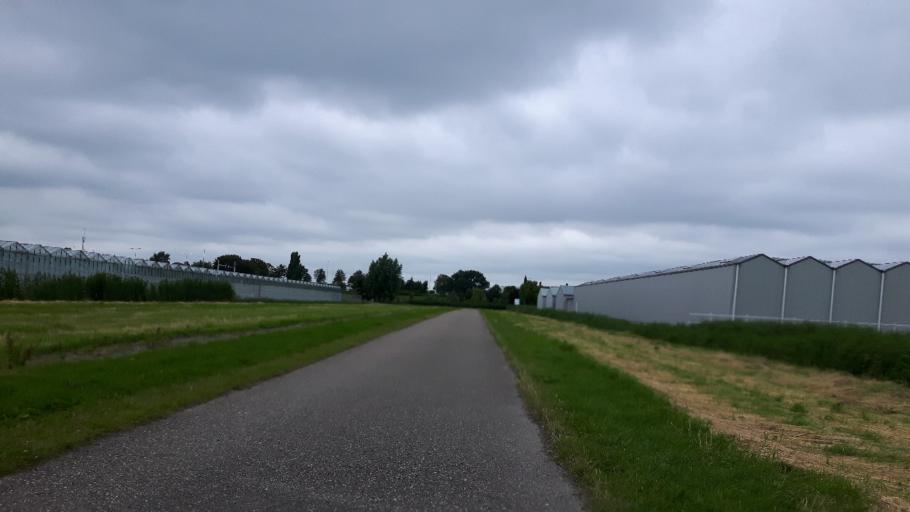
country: NL
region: South Holland
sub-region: Gemeente Lansingerland
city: Bleiswijk
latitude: 51.9930
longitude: 4.5261
